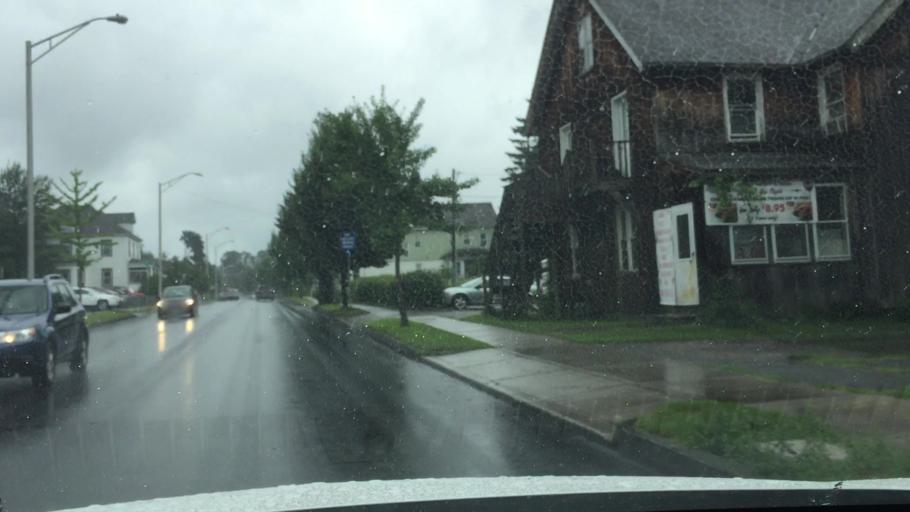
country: US
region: Massachusetts
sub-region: Berkshire County
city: Pittsfield
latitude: 42.4597
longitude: -73.2517
